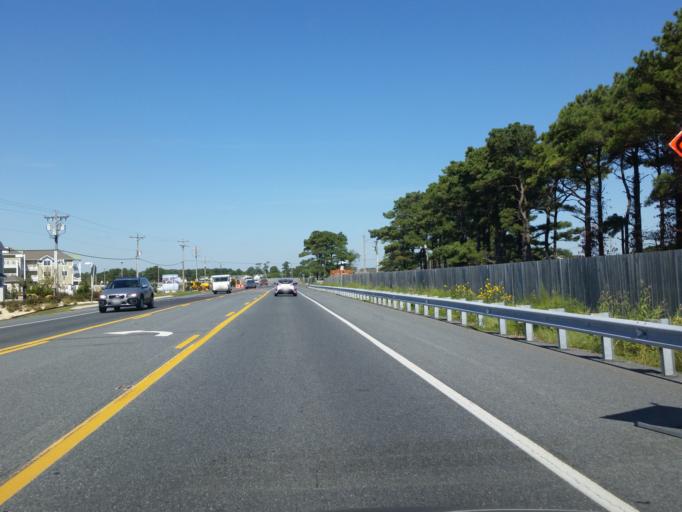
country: US
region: Delaware
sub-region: Sussex County
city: Bethany Beach
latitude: 38.4615
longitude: -75.0785
